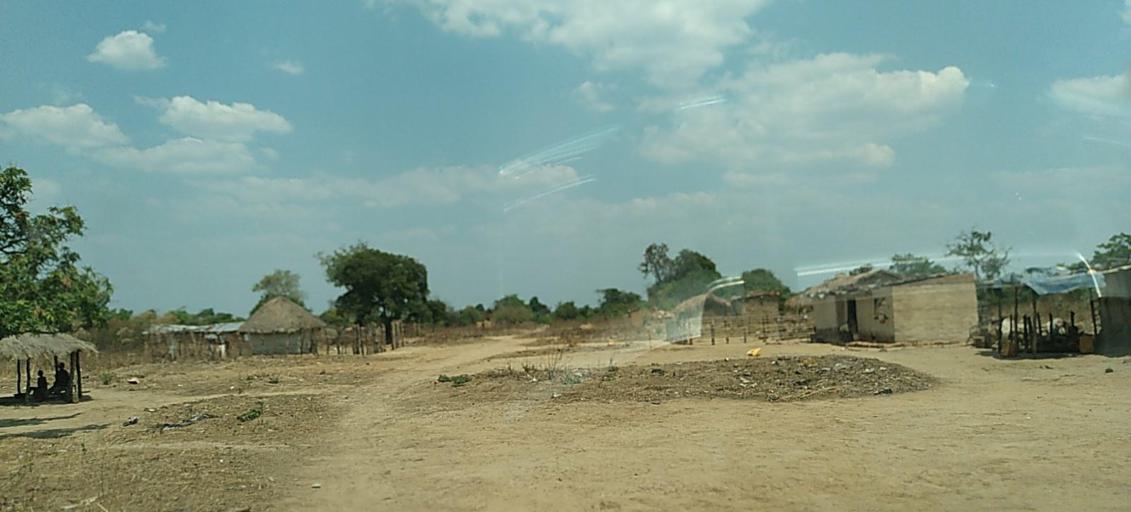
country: CD
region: Katanga
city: Kipushi
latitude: -11.9972
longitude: 27.4202
